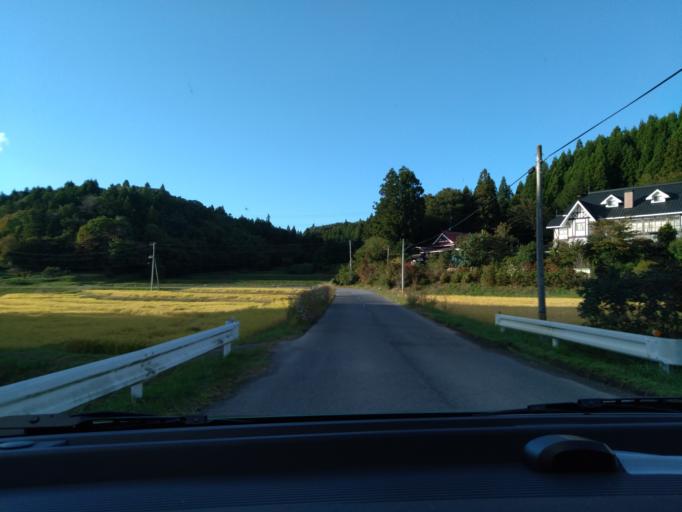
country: JP
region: Iwate
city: Ichinoseki
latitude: 38.8695
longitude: 141.1751
